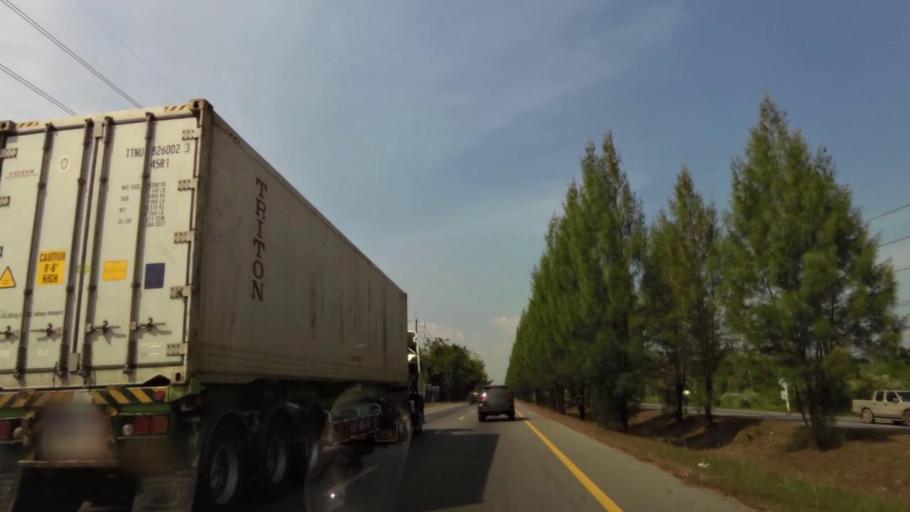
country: TH
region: Chanthaburi
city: Chanthaburi
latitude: 12.6540
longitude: 102.1263
